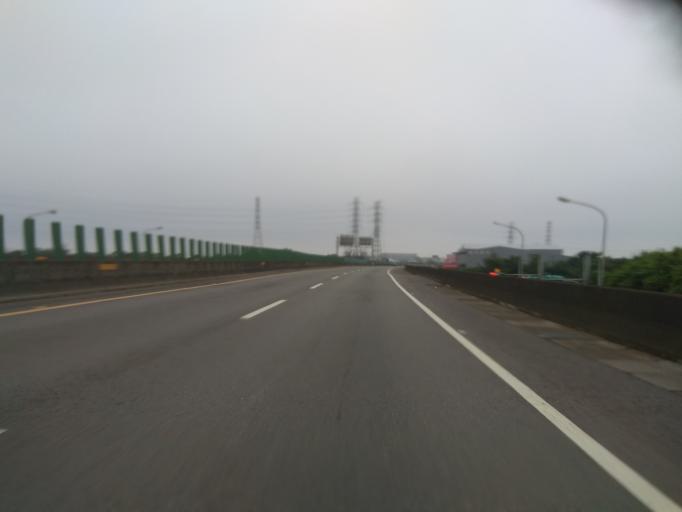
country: TW
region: Taiwan
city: Taoyuan City
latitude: 24.9844
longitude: 121.1284
